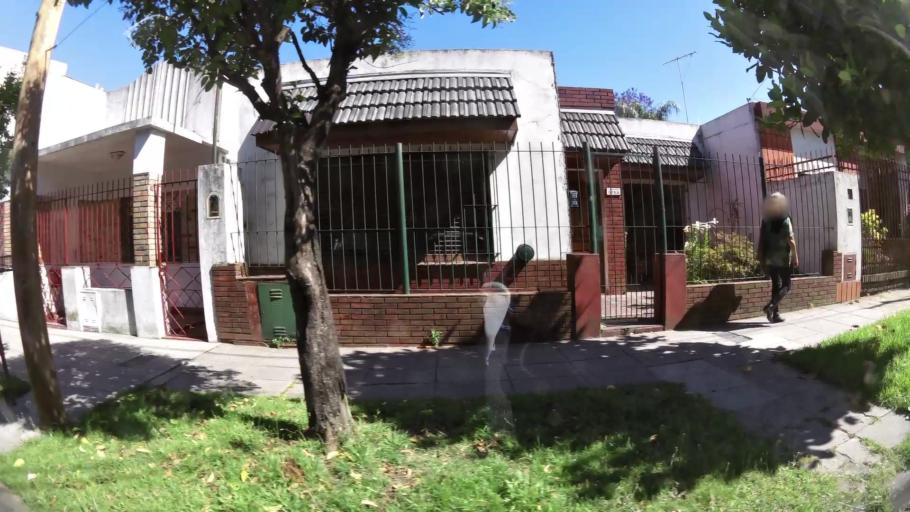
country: AR
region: Buenos Aires
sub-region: Partido de General San Martin
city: General San Martin
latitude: -34.5353
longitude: -58.5277
